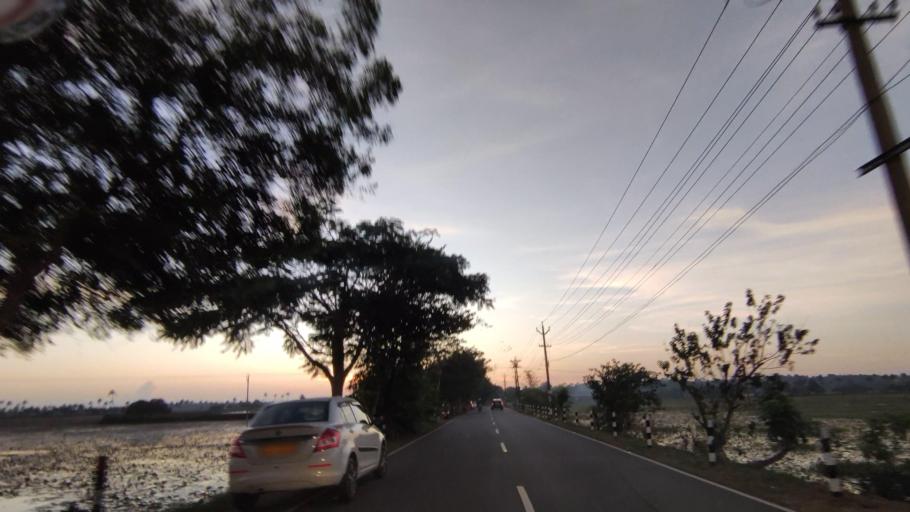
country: IN
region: Kerala
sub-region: Kottayam
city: Kottayam
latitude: 9.6912
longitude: 76.4957
